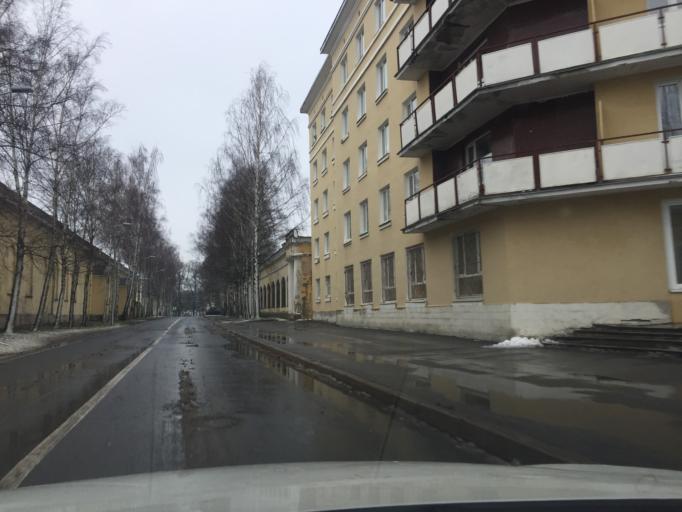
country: RU
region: St.-Petersburg
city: Pushkin
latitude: 59.7068
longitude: 30.3949
